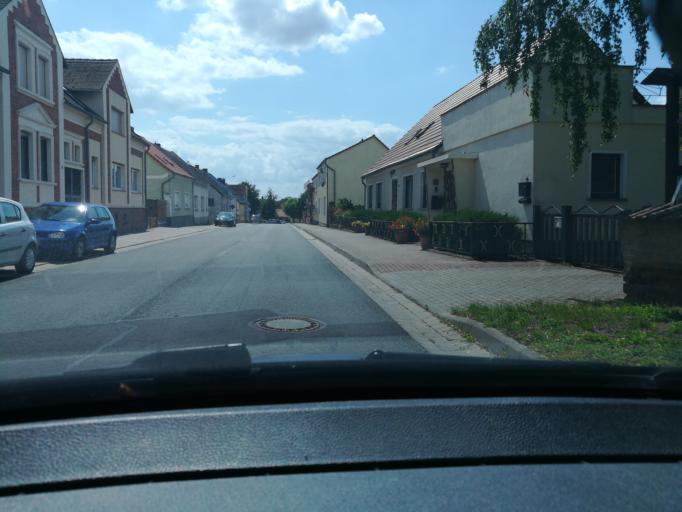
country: DE
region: Saxony-Anhalt
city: Rogatz
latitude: 52.3204
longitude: 11.7695
